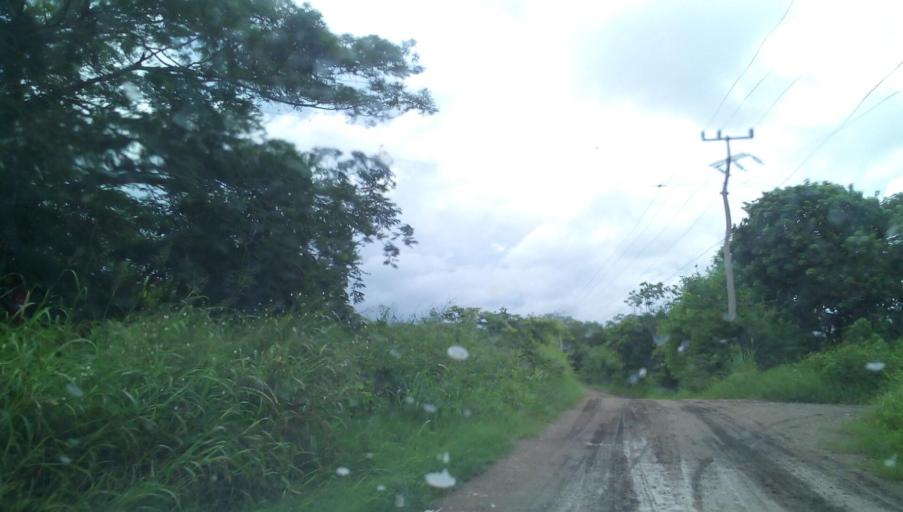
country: MX
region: Veracruz
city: Panuco
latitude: 21.8437
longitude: -98.1373
